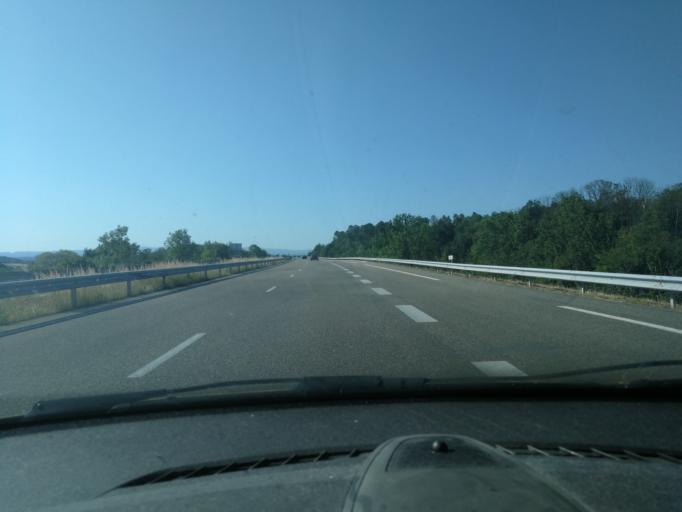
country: FR
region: Alsace
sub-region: Departement du Bas-Rhin
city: Sarrewerden
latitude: 48.8765
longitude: 7.1195
